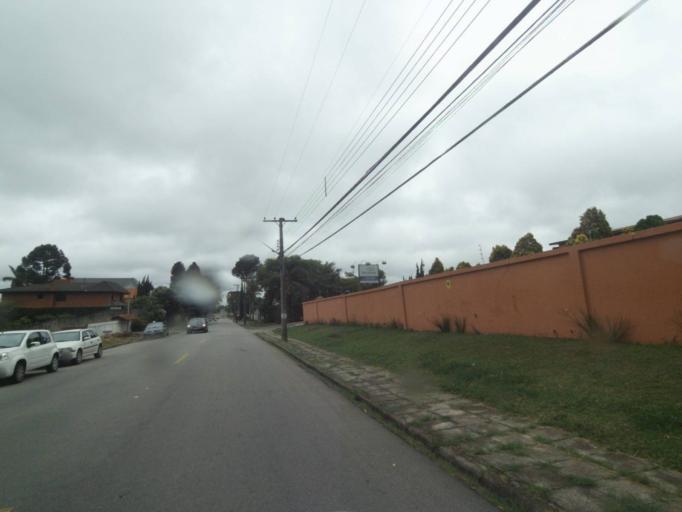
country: BR
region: Parana
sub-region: Curitiba
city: Curitiba
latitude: -25.4216
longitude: -49.3341
